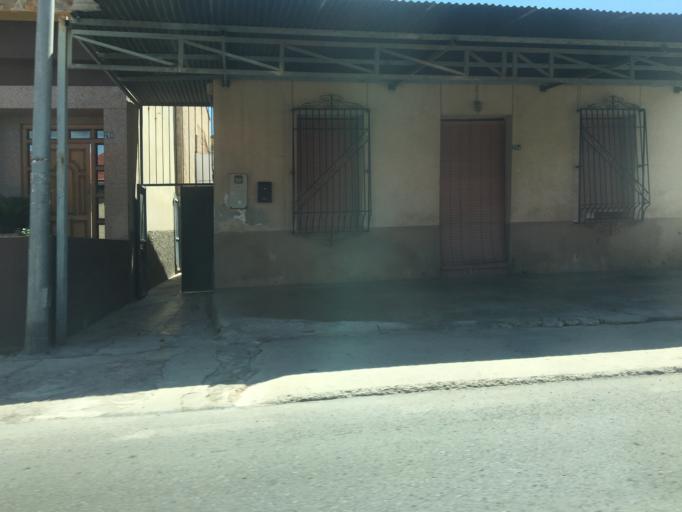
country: ES
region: Murcia
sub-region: Murcia
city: Murcia
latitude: 37.9987
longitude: -1.0878
